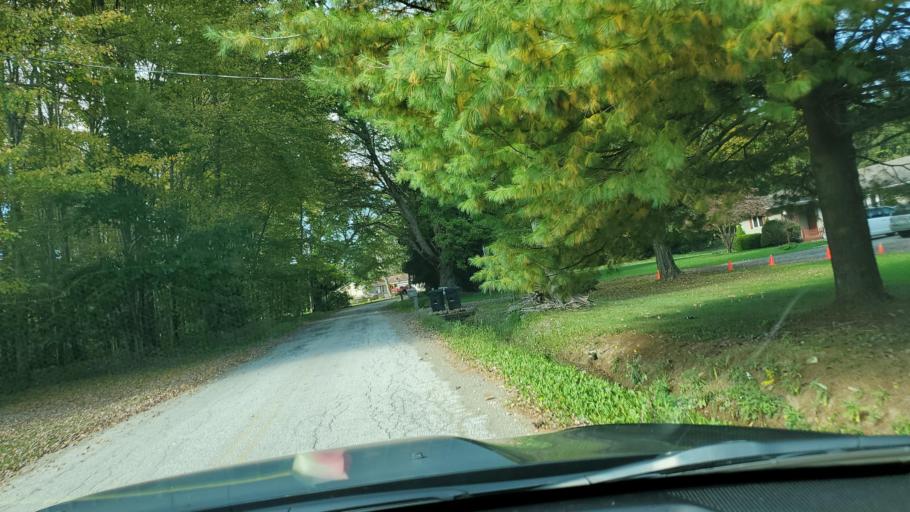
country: US
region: Ohio
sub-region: Trumbull County
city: Cortland
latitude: 41.4038
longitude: -80.6235
